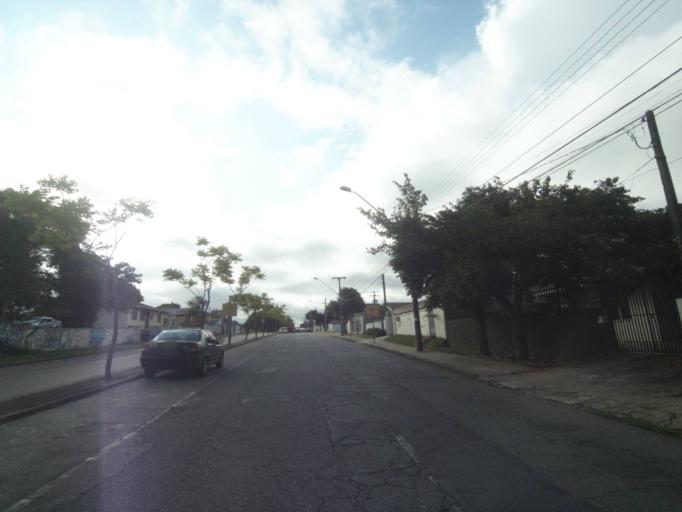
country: BR
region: Parana
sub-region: Pinhais
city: Pinhais
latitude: -25.4420
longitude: -49.2168
